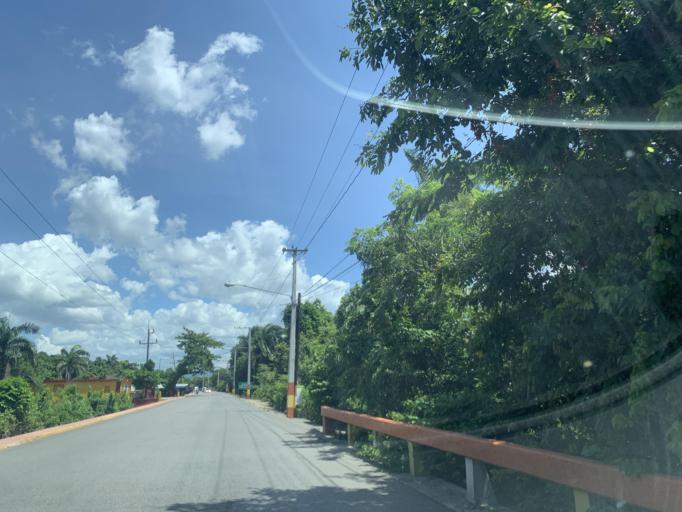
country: DO
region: Puerto Plata
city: Cabarete
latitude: 19.7053
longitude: -70.3839
